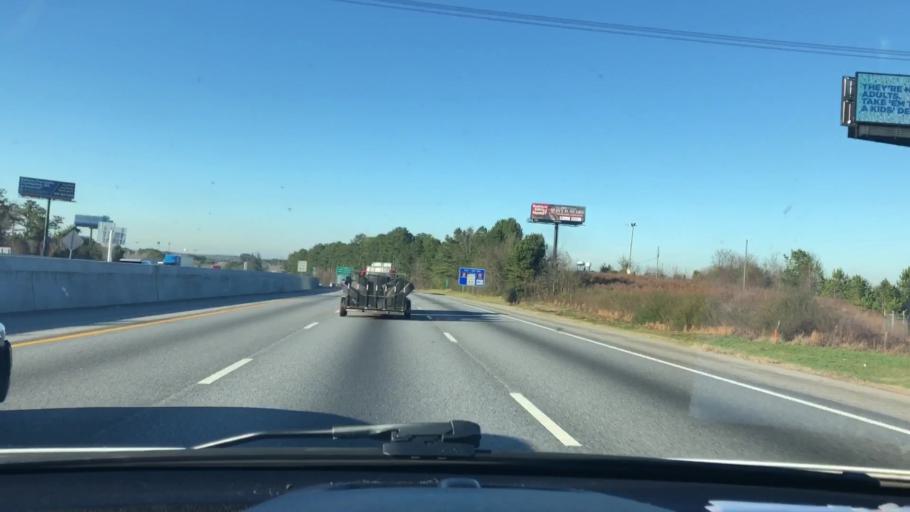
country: US
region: Georgia
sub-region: Henry County
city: Stockbridge
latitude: 33.4917
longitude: -84.2194
